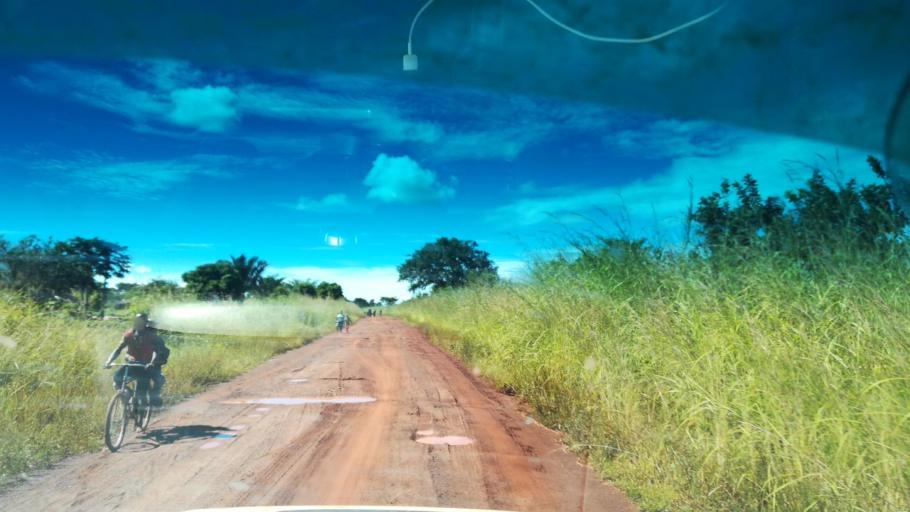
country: ZM
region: Luapula
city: Nchelenge
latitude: -9.6201
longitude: 28.2570
